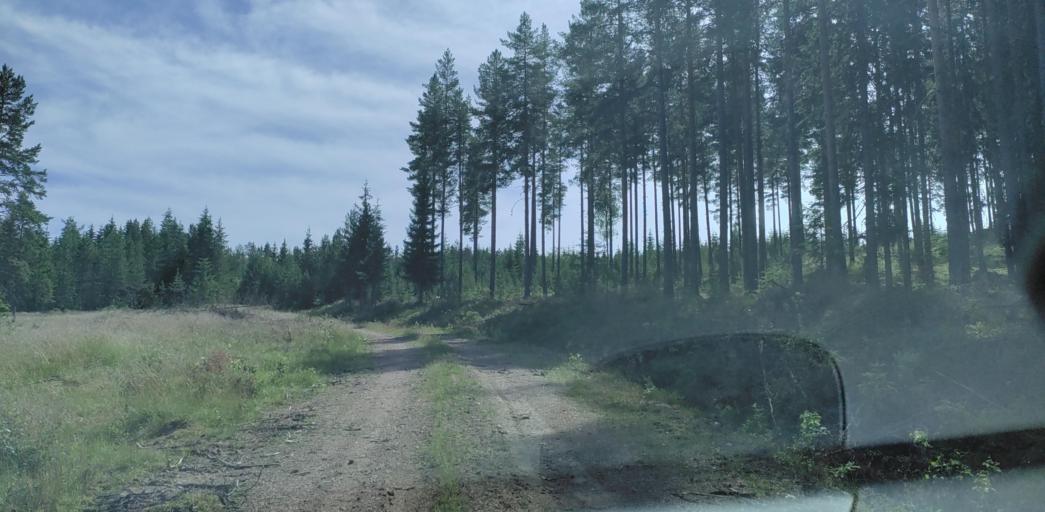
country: SE
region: Vaermland
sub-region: Hagfors Kommun
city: Ekshaerad
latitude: 60.0952
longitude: 13.3735
